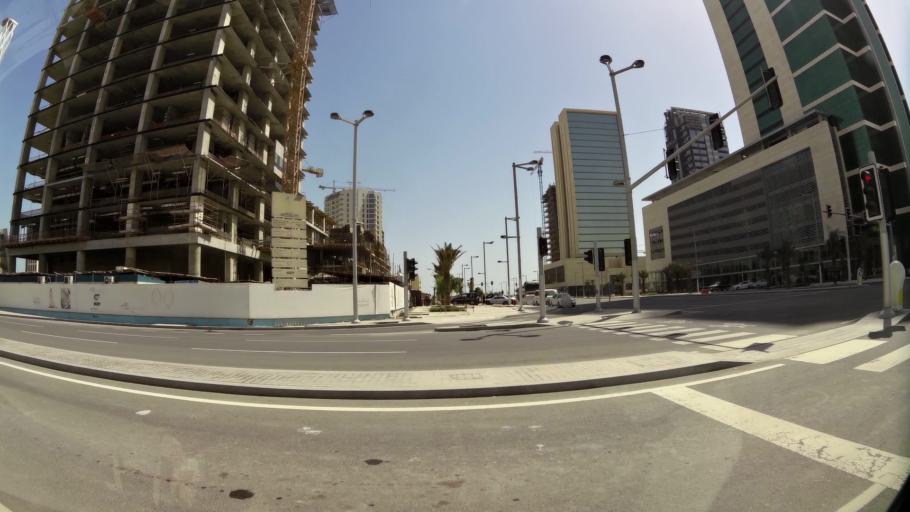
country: QA
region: Baladiyat ad Dawhah
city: Doha
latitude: 25.3894
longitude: 51.5200
